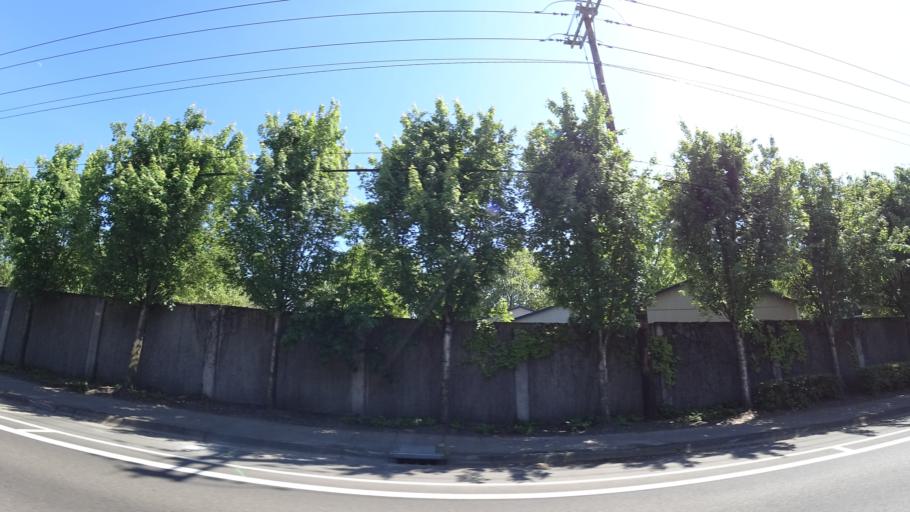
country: US
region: Oregon
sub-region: Washington County
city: Tigard
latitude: 45.4448
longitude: -122.7977
